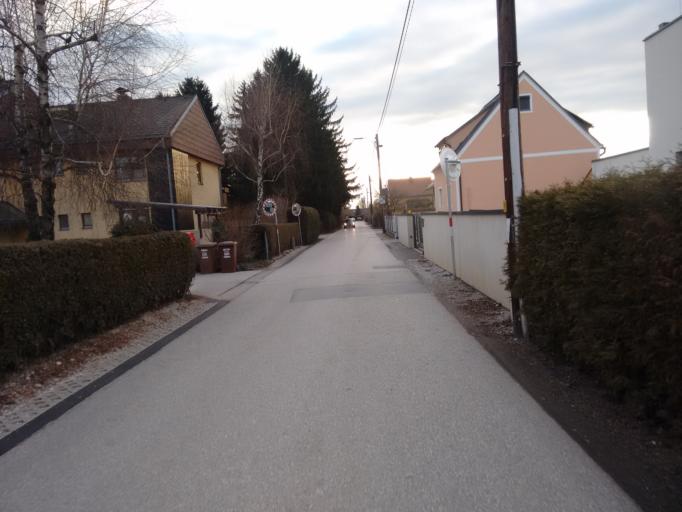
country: AT
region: Styria
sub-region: Graz Stadt
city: Graz
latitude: 47.0453
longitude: 15.4713
